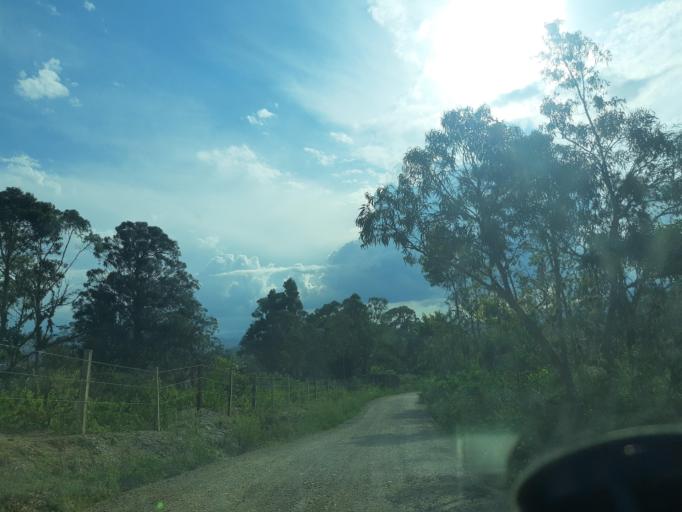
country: CO
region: Boyaca
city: Villa de Leiva
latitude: 5.6641
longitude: -73.5696
